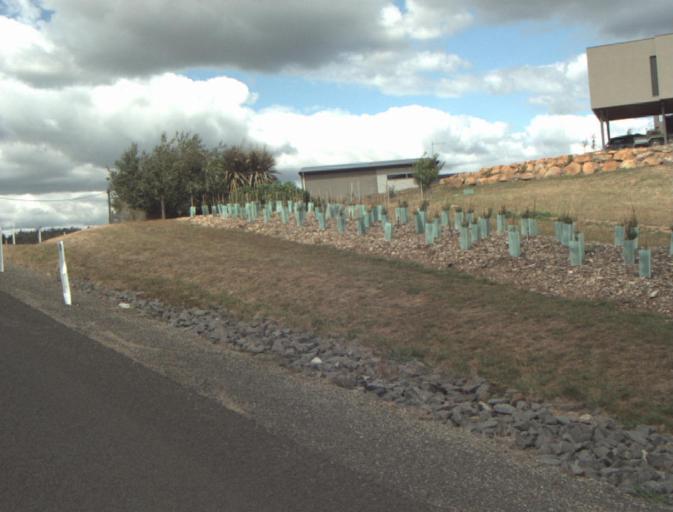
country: AU
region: Tasmania
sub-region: Launceston
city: Mayfield
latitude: -41.3002
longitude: 147.0448
